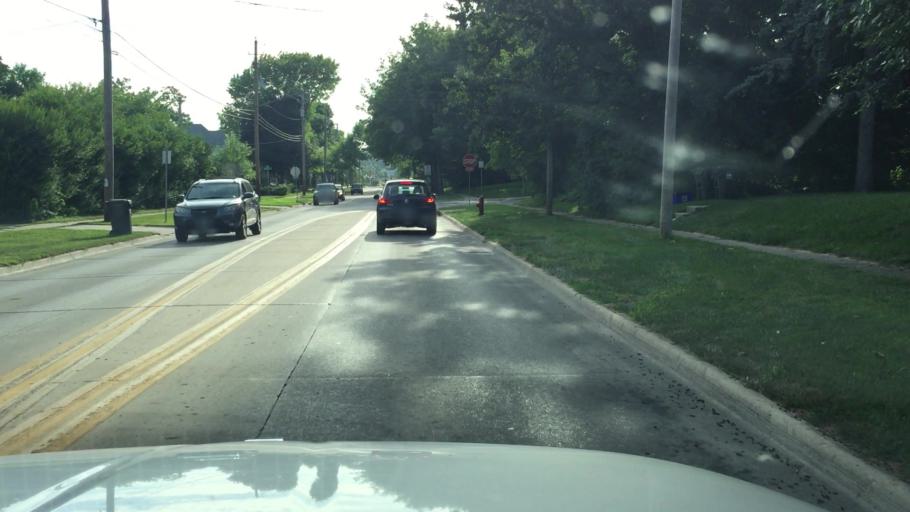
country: US
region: Iowa
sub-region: Johnson County
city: Iowa City
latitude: 41.6495
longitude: -91.5254
